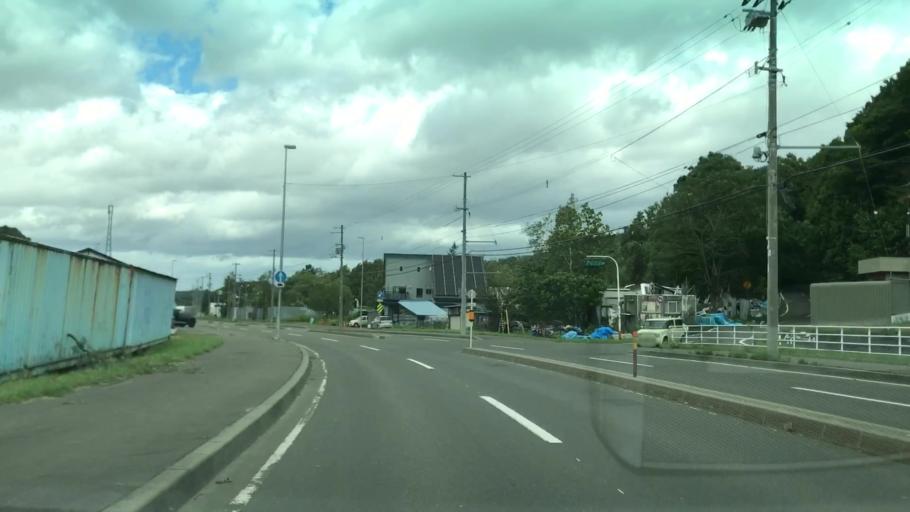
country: JP
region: Hokkaido
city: Kitahiroshima
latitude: 42.9678
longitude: 141.4550
